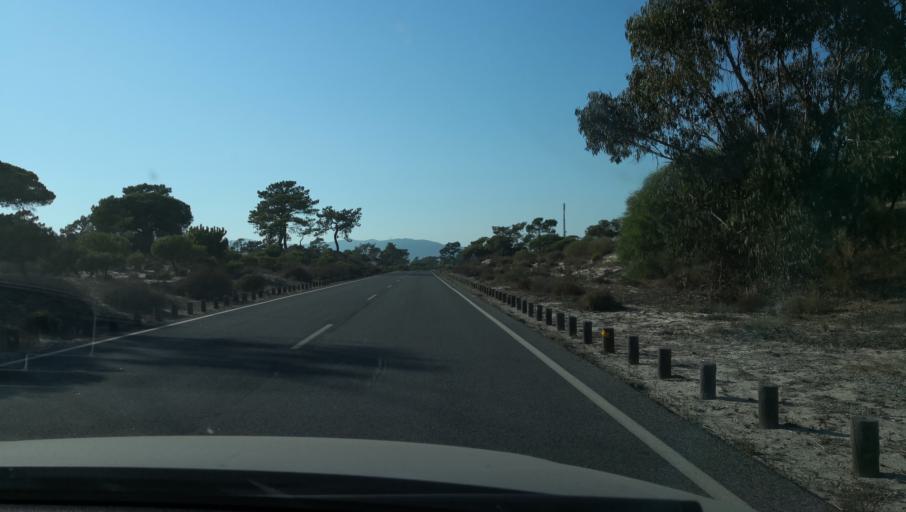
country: PT
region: Setubal
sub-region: Setubal
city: Setubal
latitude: 38.4680
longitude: -8.8793
